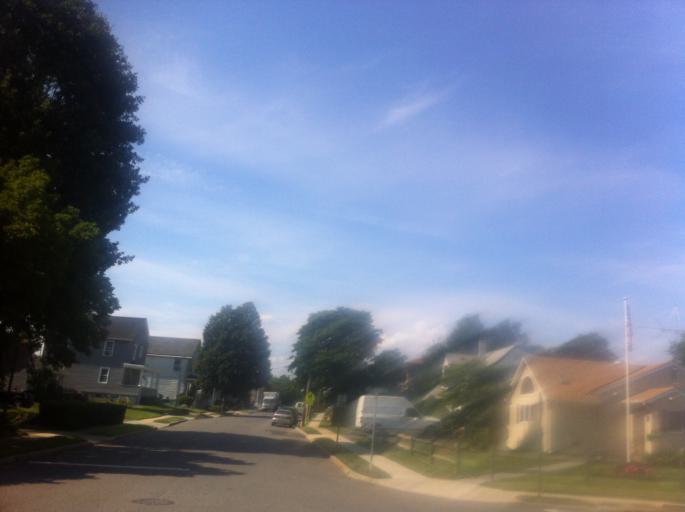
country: US
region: New York
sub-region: Nassau County
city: Locust Valley
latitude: 40.8553
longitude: -73.6072
